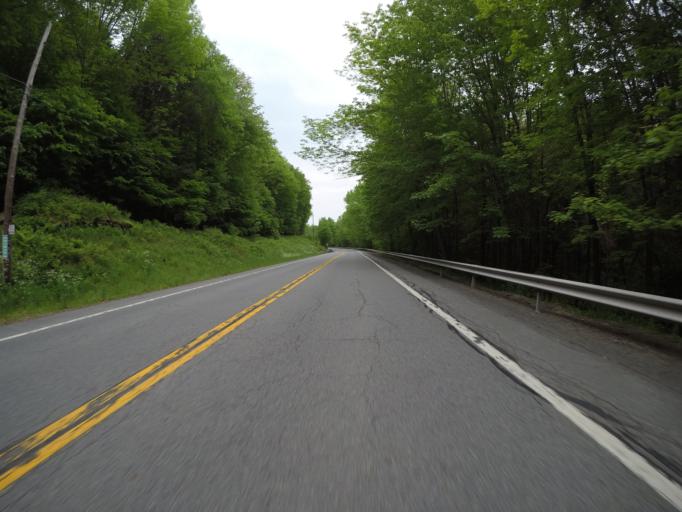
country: US
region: New York
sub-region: Sullivan County
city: Livingston Manor
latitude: 42.0715
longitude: -74.8870
